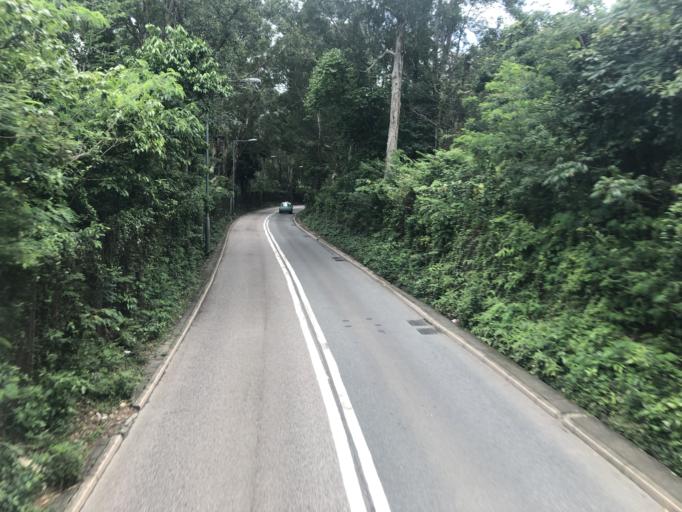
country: HK
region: Tai Po
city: Tai Po
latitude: 22.4882
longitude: 114.1165
